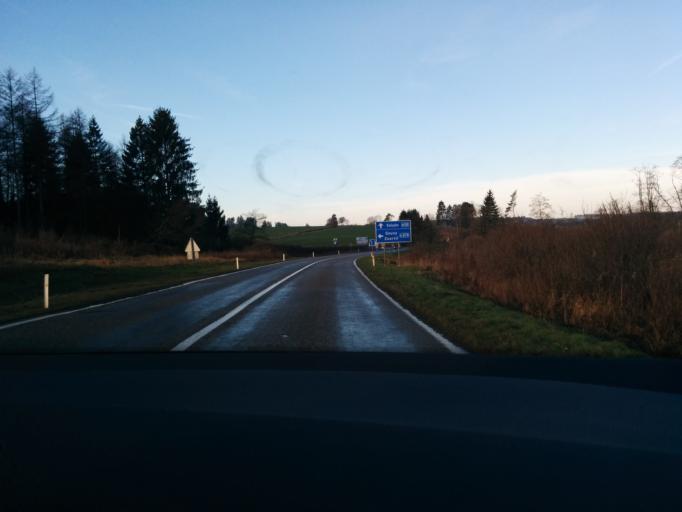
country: BE
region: Wallonia
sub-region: Province du Luxembourg
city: Gouvy
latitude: 50.2217
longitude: 5.9409
